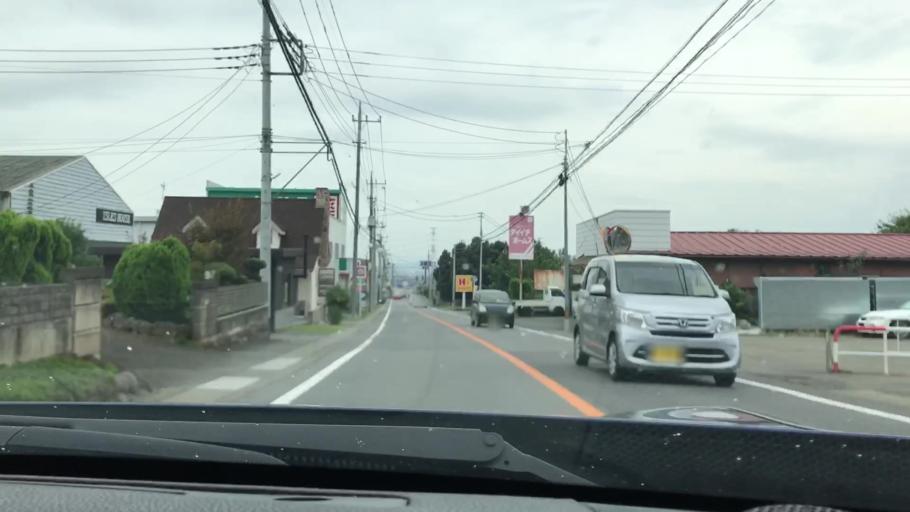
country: JP
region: Gunma
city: Kanekomachi
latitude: 36.3913
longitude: 138.9613
